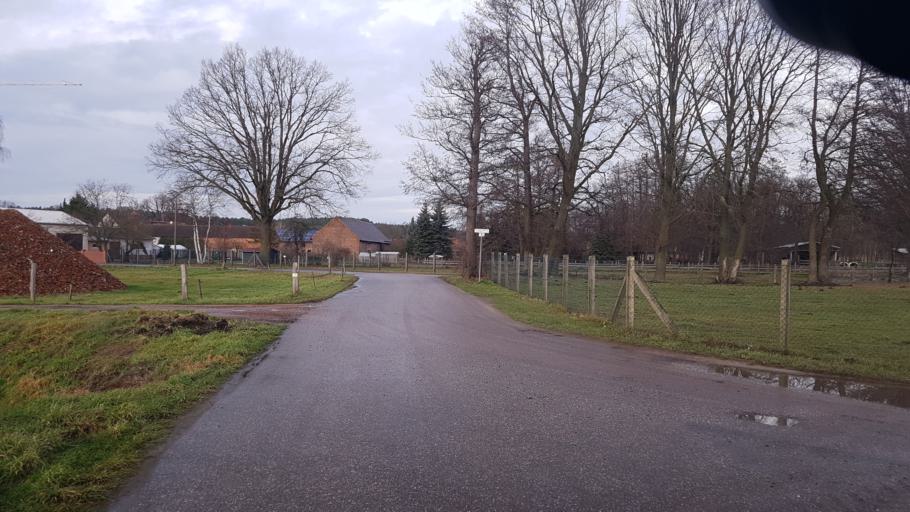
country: DE
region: Brandenburg
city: Hohenbucko
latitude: 51.7350
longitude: 13.4421
